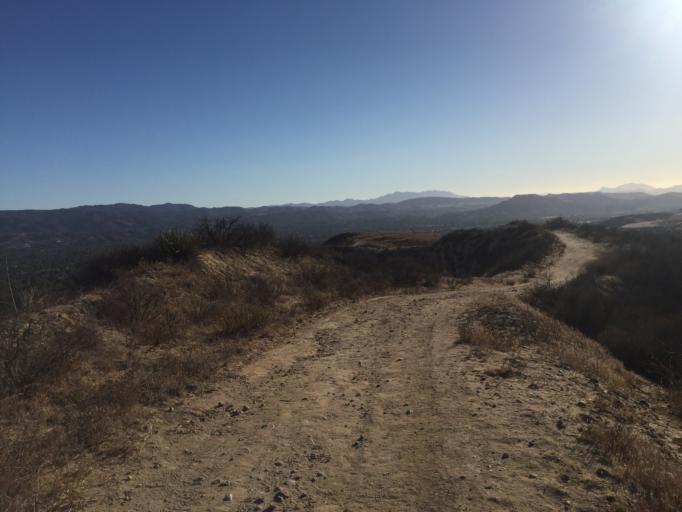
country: US
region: California
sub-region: Ventura County
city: Simi Valley
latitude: 34.2951
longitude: -118.7528
